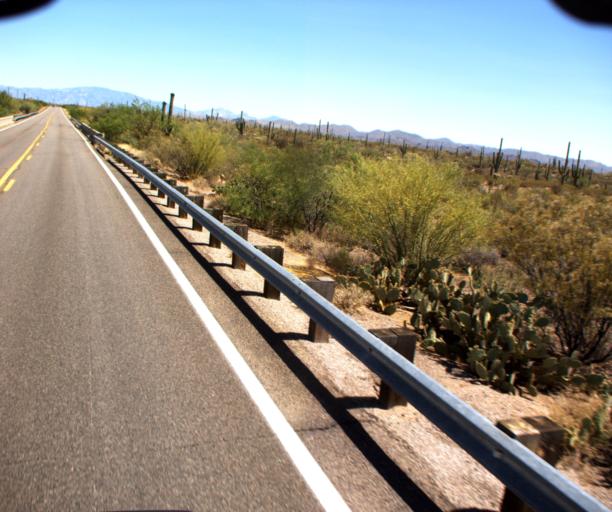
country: US
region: Arizona
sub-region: Pima County
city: Catalina
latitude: 32.6944
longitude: -111.0861
